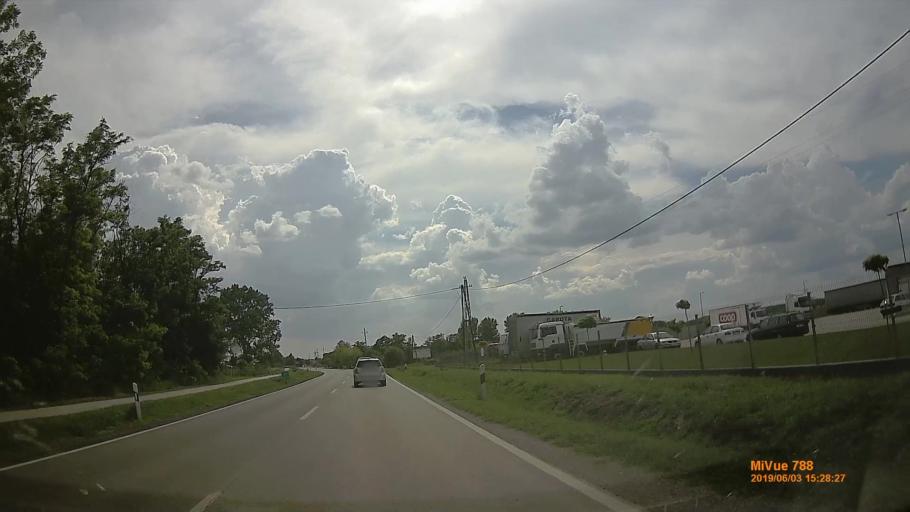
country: HU
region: Bacs-Kiskun
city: Soltvadkert
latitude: 46.5908
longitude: 19.4054
